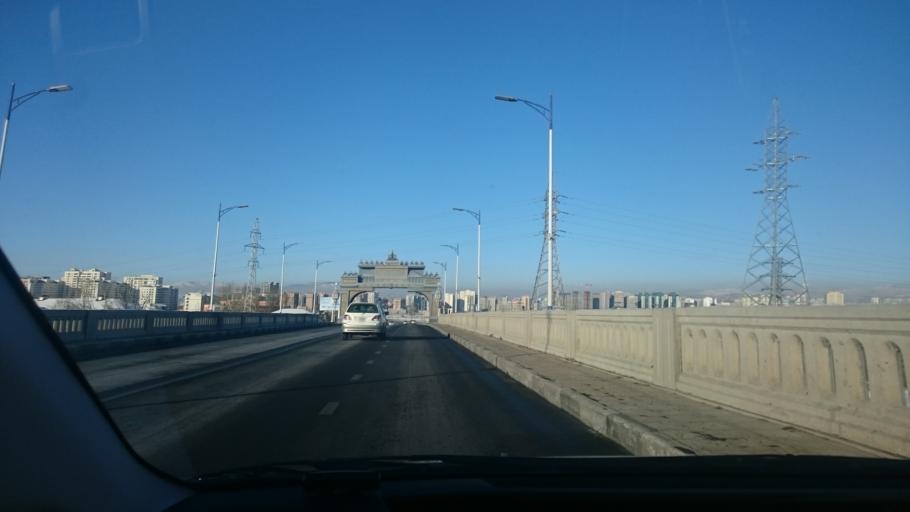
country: MN
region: Ulaanbaatar
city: Ulaanbaatar
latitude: 47.8876
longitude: 106.9394
